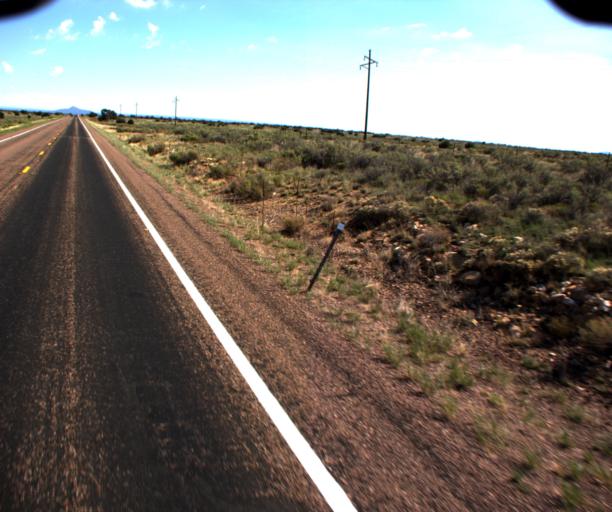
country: US
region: Arizona
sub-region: Coconino County
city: Williams
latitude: 35.5777
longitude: -112.1532
